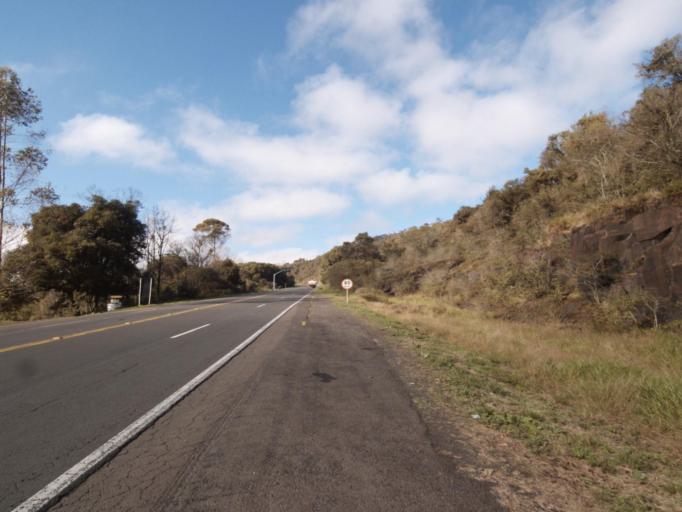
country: BR
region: Rio Grande do Sul
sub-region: Frederico Westphalen
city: Frederico Westphalen
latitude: -27.0807
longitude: -53.2242
